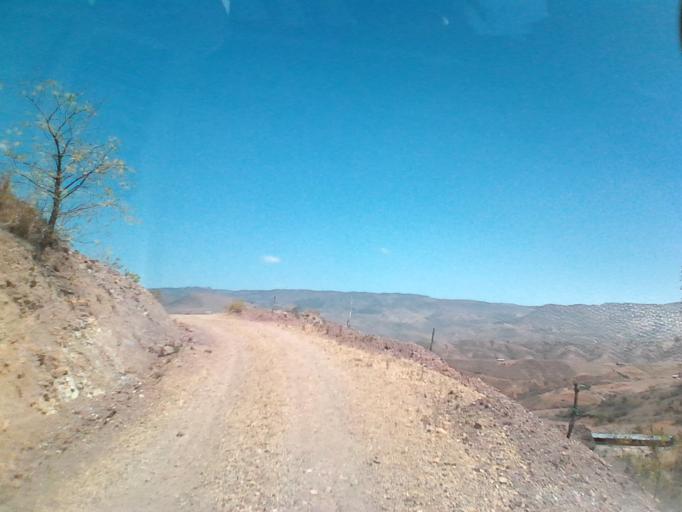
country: CO
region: Boyaca
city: Sachica
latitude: 5.5981
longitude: -73.5726
